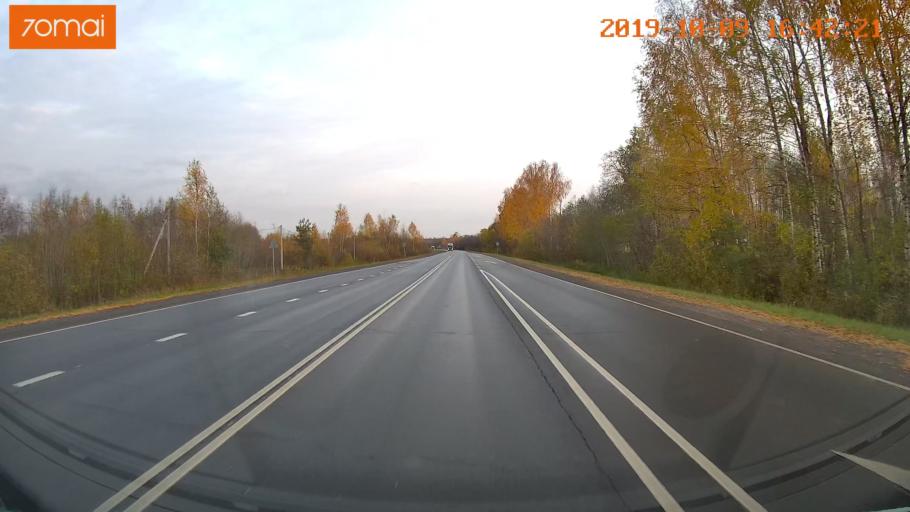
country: RU
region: Kostroma
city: Volgorechensk
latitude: 57.4631
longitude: 41.0984
